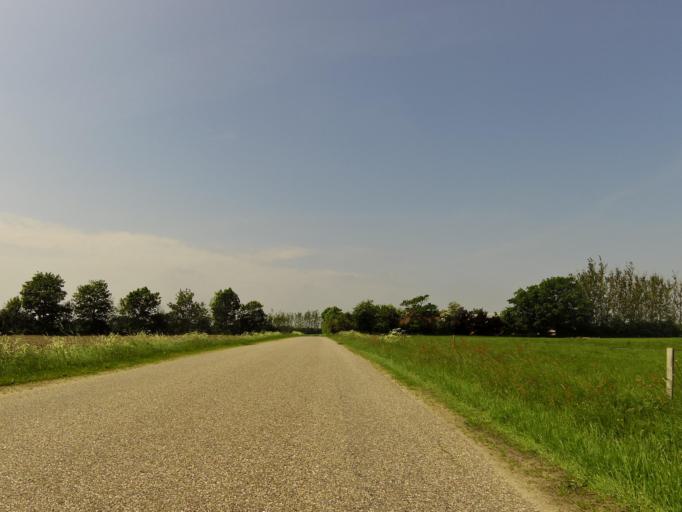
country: DK
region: South Denmark
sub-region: Tonder Kommune
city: Toftlund
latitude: 55.1892
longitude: 9.0280
